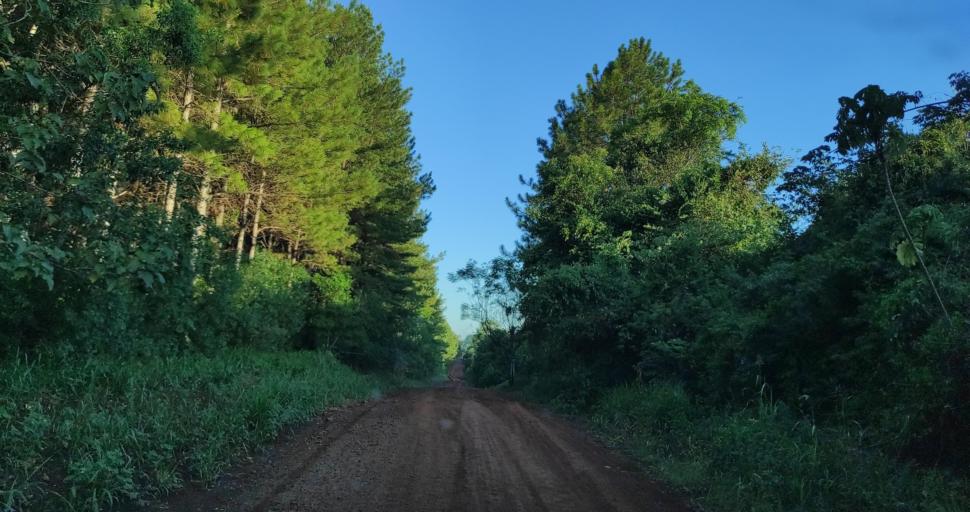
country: AR
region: Misiones
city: Gobernador Roca
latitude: -27.2211
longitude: -55.4353
